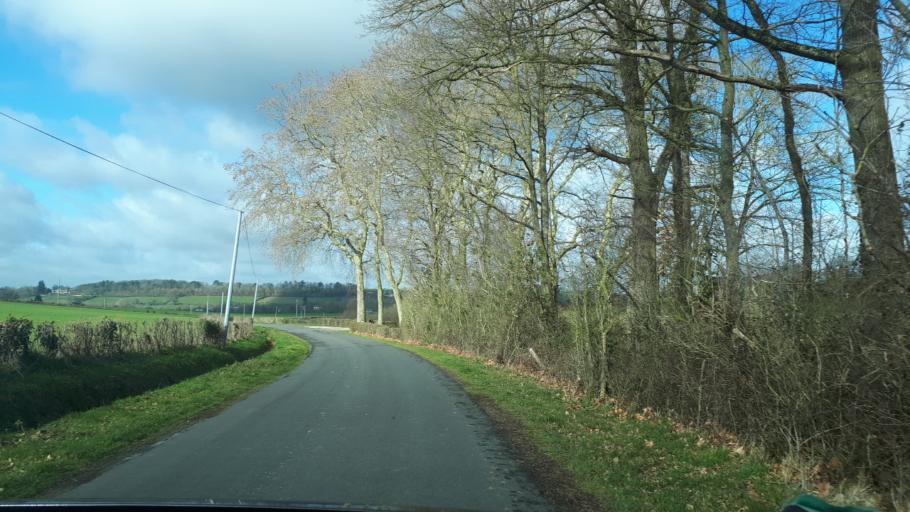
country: FR
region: Centre
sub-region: Departement du Loir-et-Cher
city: Sarge-sur-Braye
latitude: 47.9165
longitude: 0.8616
